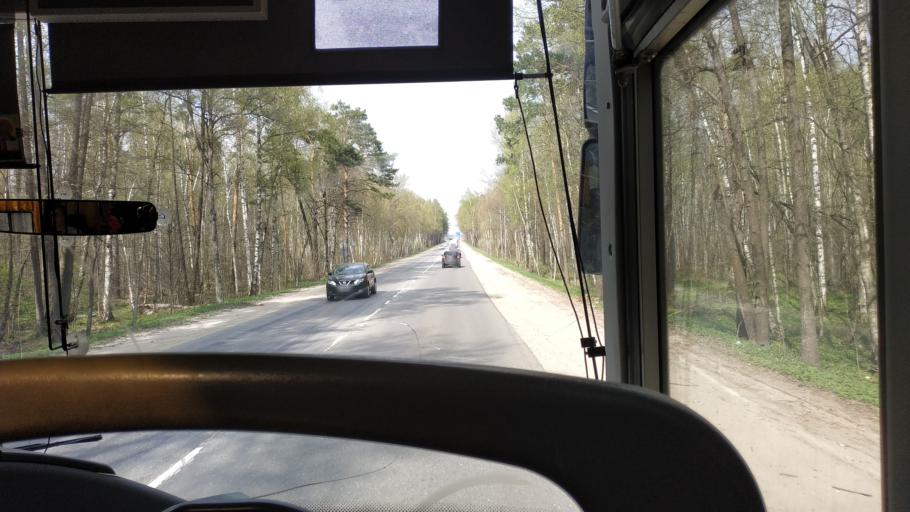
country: RU
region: Moskovskaya
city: Lytkarino
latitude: 55.6055
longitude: 37.9168
